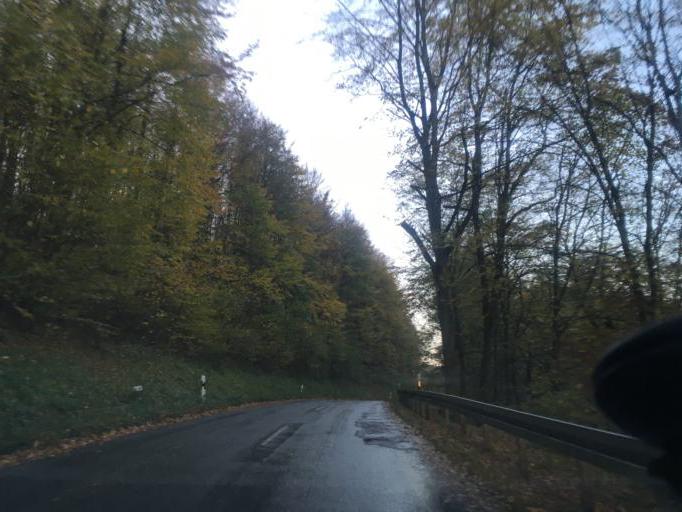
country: DE
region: Lower Saxony
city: Bodenfelde
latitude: 51.6249
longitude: 9.5979
